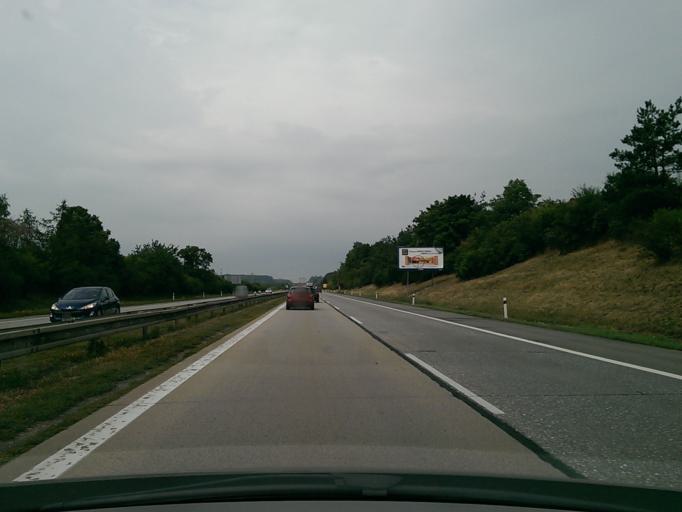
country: CZ
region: South Moravian
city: Ricany
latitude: 49.2455
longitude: 16.3635
